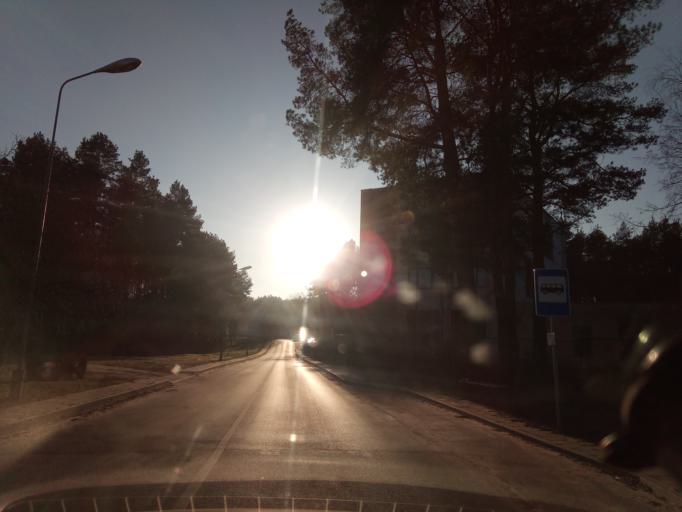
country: LT
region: Alytaus apskritis
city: Druskininkai
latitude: 54.0043
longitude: 23.9806
